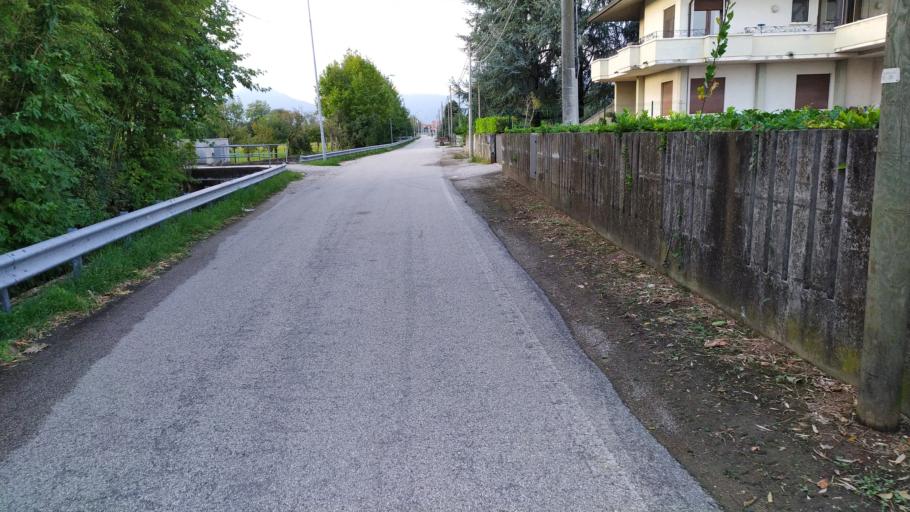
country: IT
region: Veneto
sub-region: Provincia di Vicenza
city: Novoledo
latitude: 45.6397
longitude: 11.5073
